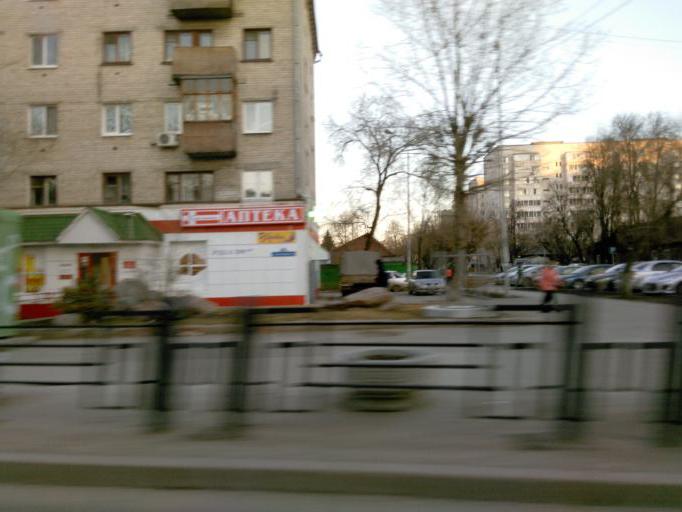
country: RU
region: Tjumen
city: Tyumen
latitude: 57.1611
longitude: 65.4984
